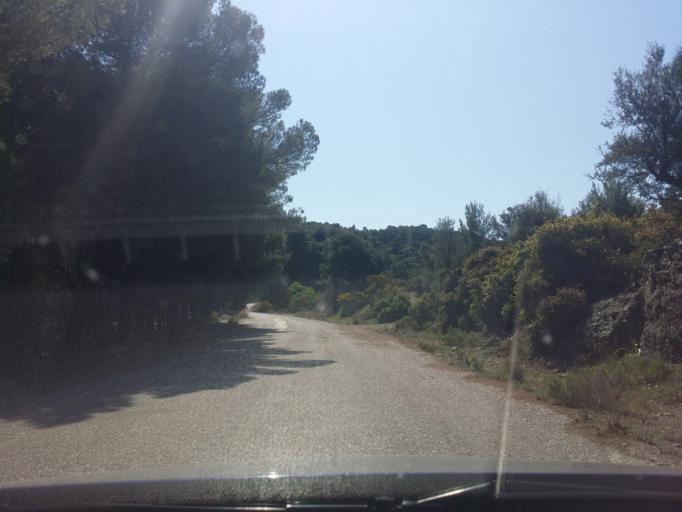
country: GR
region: Attica
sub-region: Nomos Piraios
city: Poros
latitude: 37.5221
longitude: 23.4832
